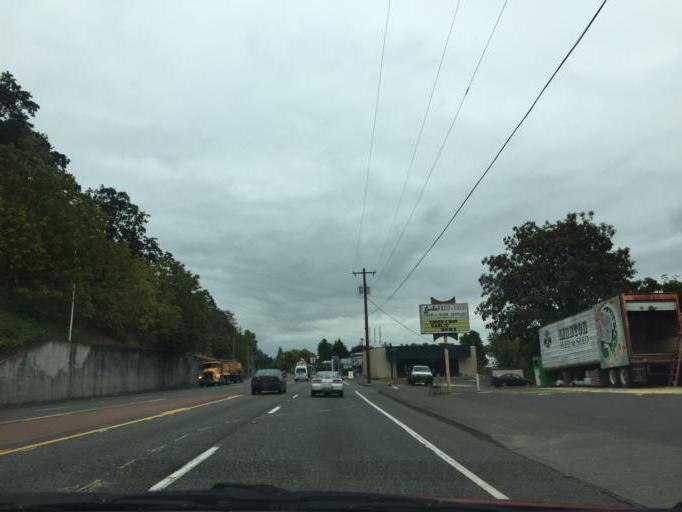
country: US
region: Oregon
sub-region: Washington County
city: Cedar Mill
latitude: 45.6002
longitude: -122.7868
